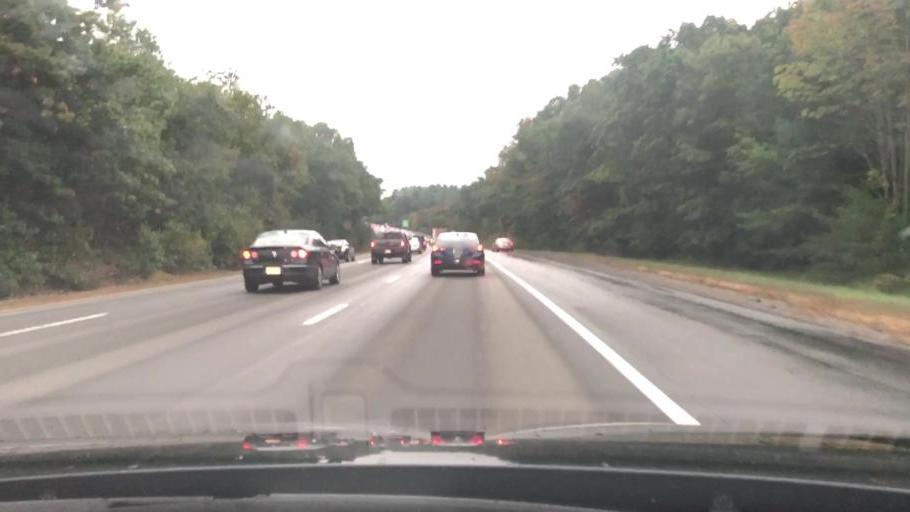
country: US
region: Massachusetts
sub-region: Middlesex County
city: Tewksbury
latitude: 42.6512
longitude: -71.2114
